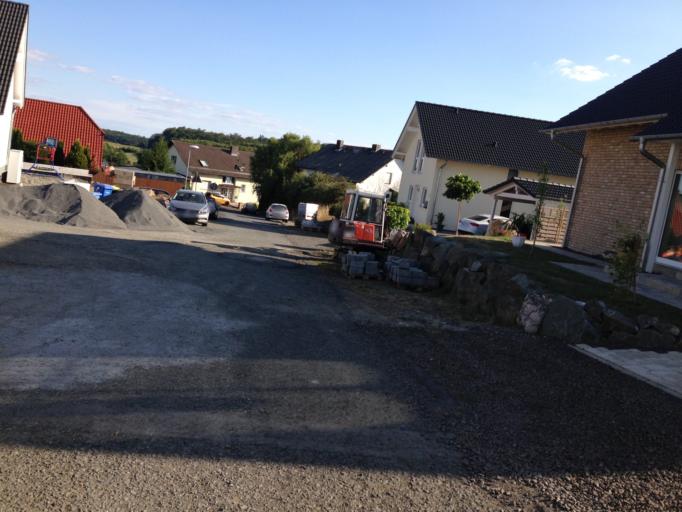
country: DE
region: Hesse
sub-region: Regierungsbezirk Giessen
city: Reiskirchen
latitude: 50.6204
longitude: 8.8502
